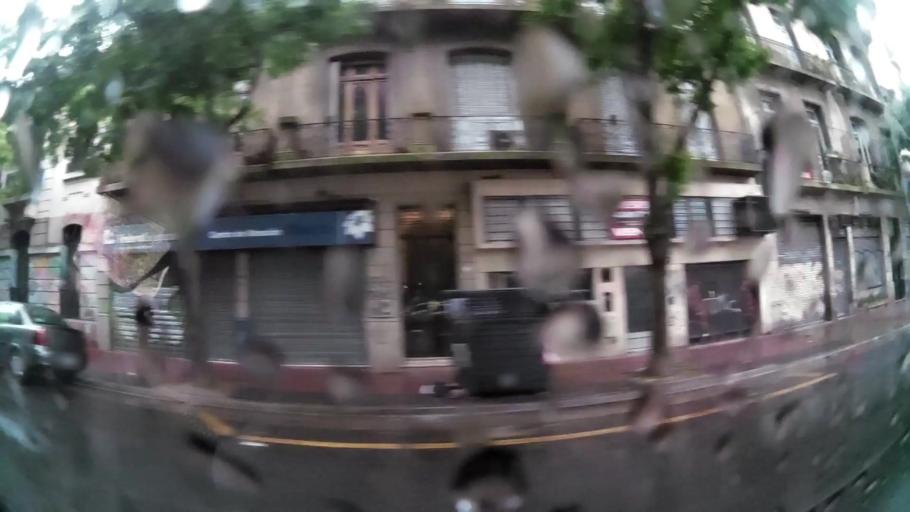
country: AR
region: Buenos Aires F.D.
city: Buenos Aires
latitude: -34.6242
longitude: -58.3701
